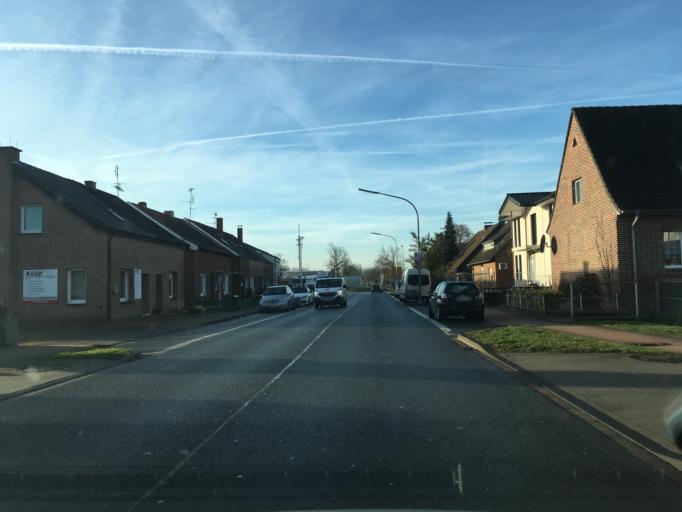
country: DE
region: North Rhine-Westphalia
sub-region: Regierungsbezirk Munster
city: Ahaus
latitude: 52.0879
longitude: 7.0228
